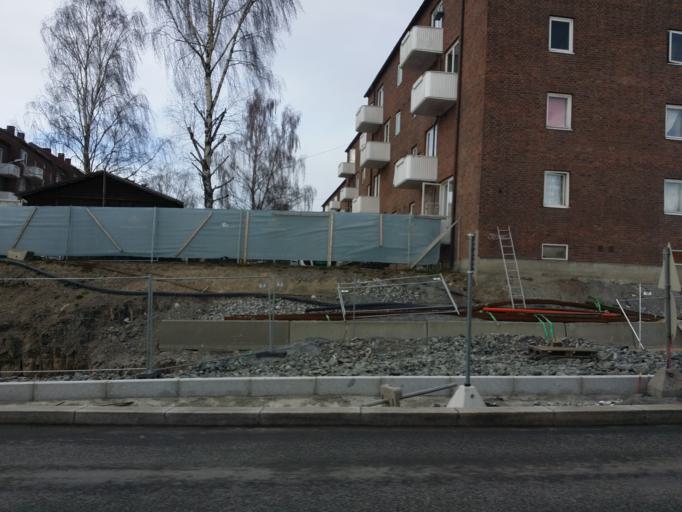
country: NO
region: Oslo
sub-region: Oslo
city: Oslo
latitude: 59.9351
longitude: 10.7908
